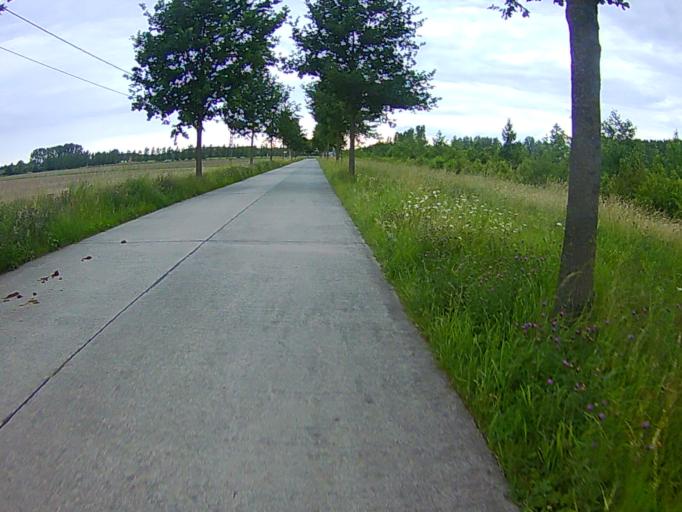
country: BE
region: Flanders
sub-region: Provincie Antwerpen
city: Lier
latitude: 51.0930
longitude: 4.5886
